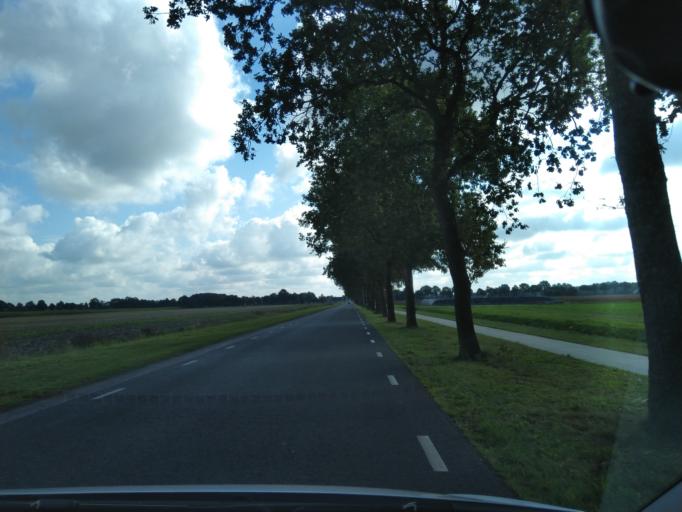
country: NL
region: Groningen
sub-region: Gemeente Pekela
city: Oude Pekela
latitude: 53.0921
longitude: 6.9644
